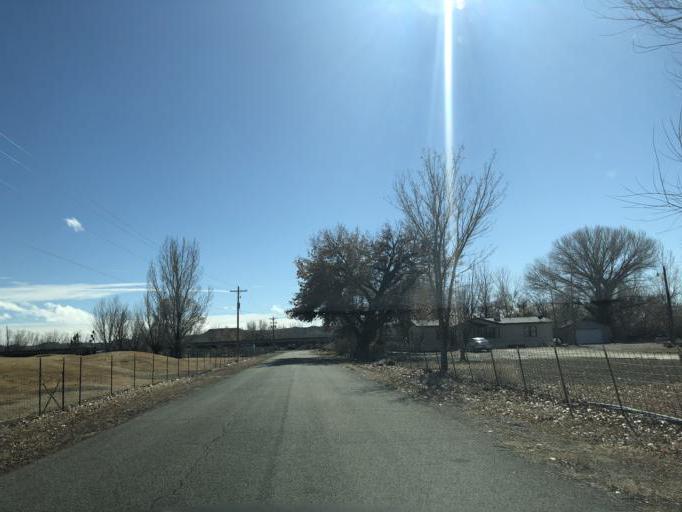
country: US
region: Utah
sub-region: Carbon County
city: East Carbon City
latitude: 38.9875
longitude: -110.1538
